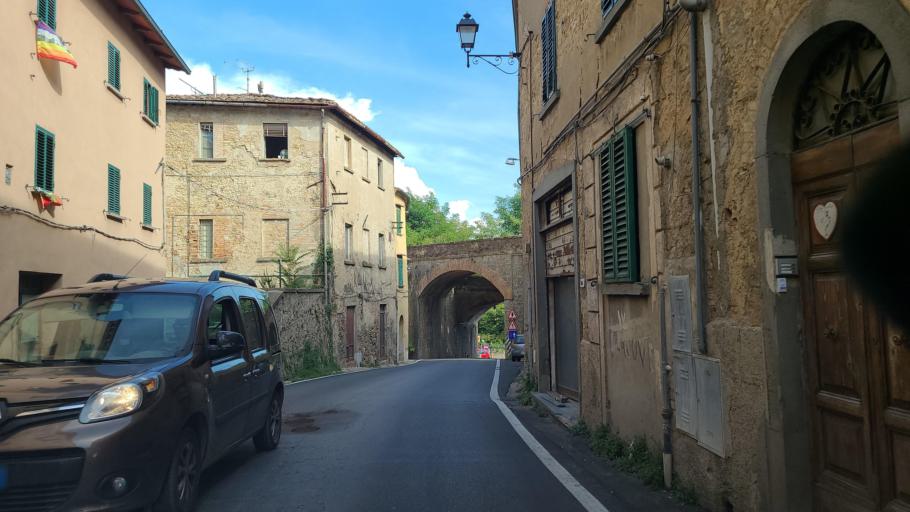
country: IT
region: Tuscany
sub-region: Province of Pisa
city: Volterra
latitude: 43.3996
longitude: 10.8714
